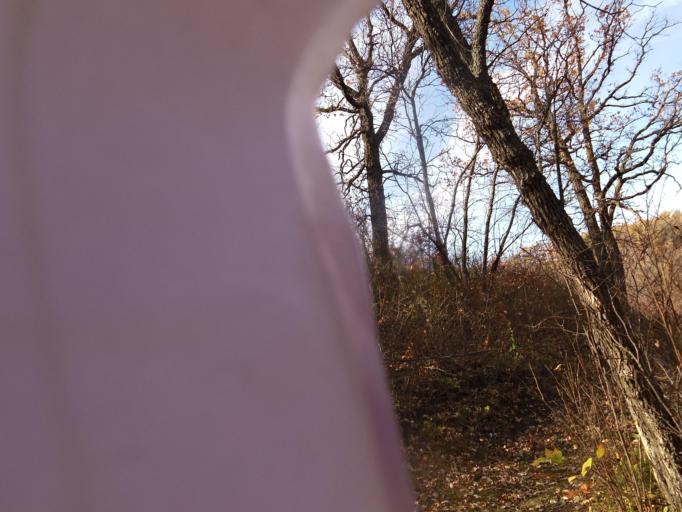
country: CA
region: Manitoba
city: Morden
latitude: 48.9471
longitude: -98.0706
